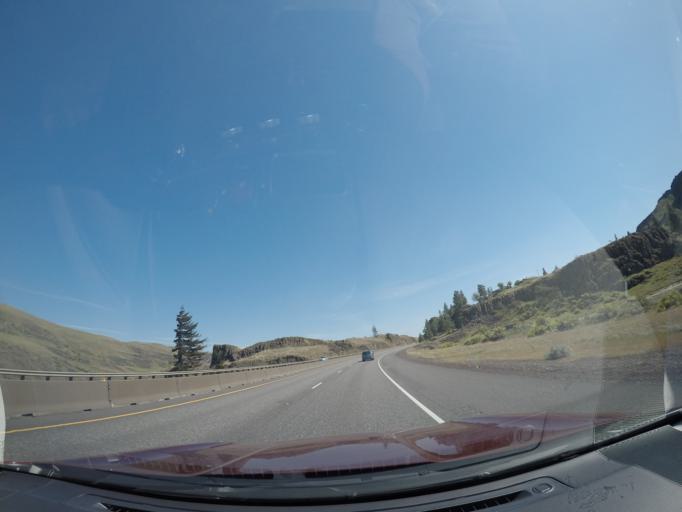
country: US
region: Oregon
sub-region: Wasco County
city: Chenoweth
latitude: 45.6651
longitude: -121.2228
